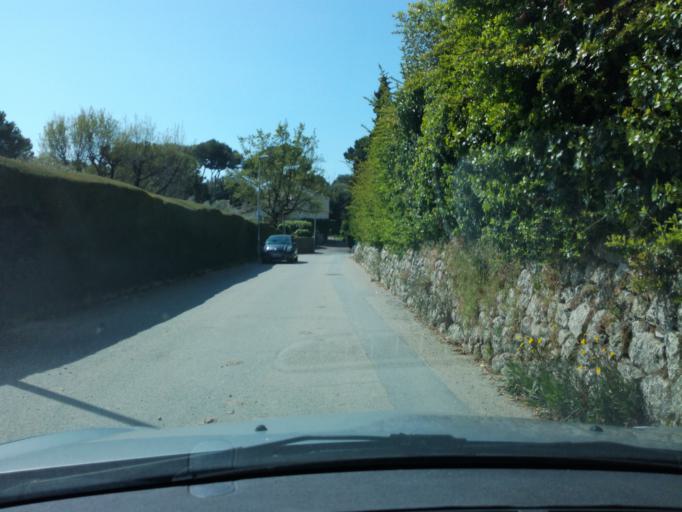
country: FR
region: Provence-Alpes-Cote d'Azur
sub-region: Departement des Alpes-Maritimes
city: Mougins
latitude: 43.6087
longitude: 6.9916
